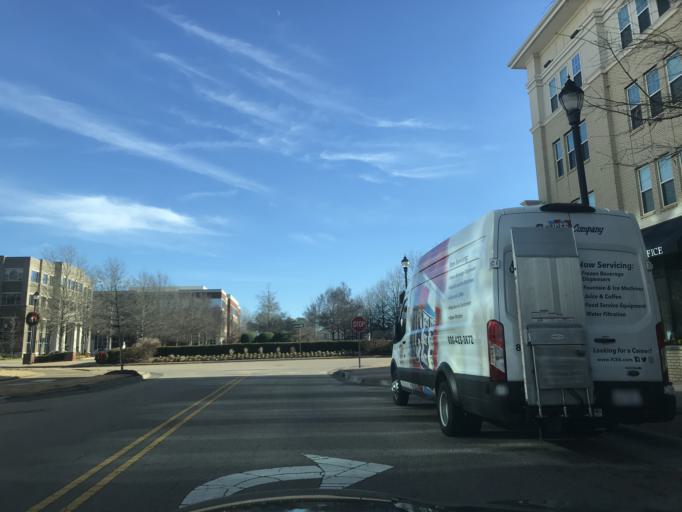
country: US
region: North Carolina
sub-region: Wake County
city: Cary
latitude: 35.8080
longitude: -78.7307
